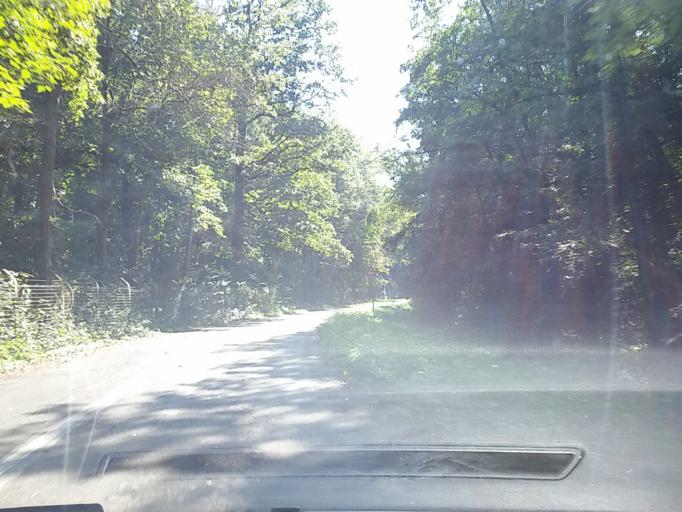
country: BE
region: Flanders
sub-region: Provincie Vlaams-Brabant
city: Machelen
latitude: 50.9239
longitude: 4.4668
